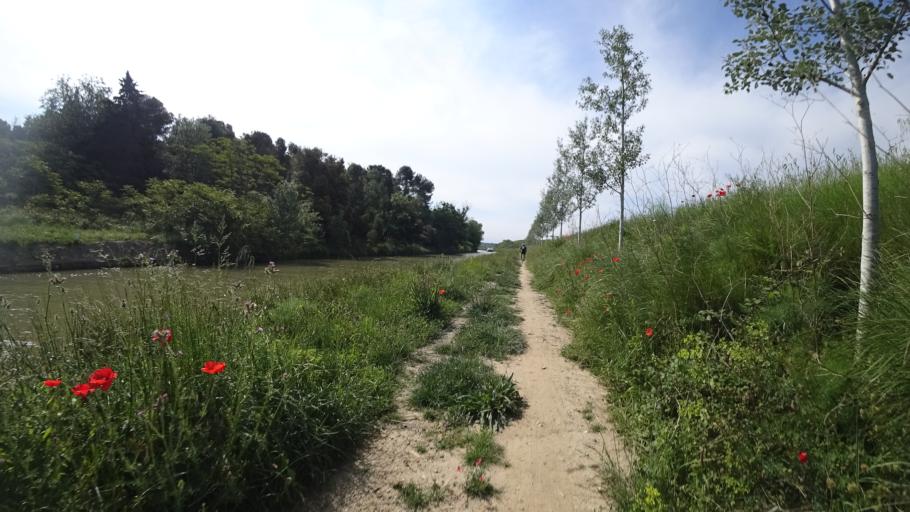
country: FR
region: Languedoc-Roussillon
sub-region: Departement de l'Herault
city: Olonzac
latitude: 43.2611
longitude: 2.7495
